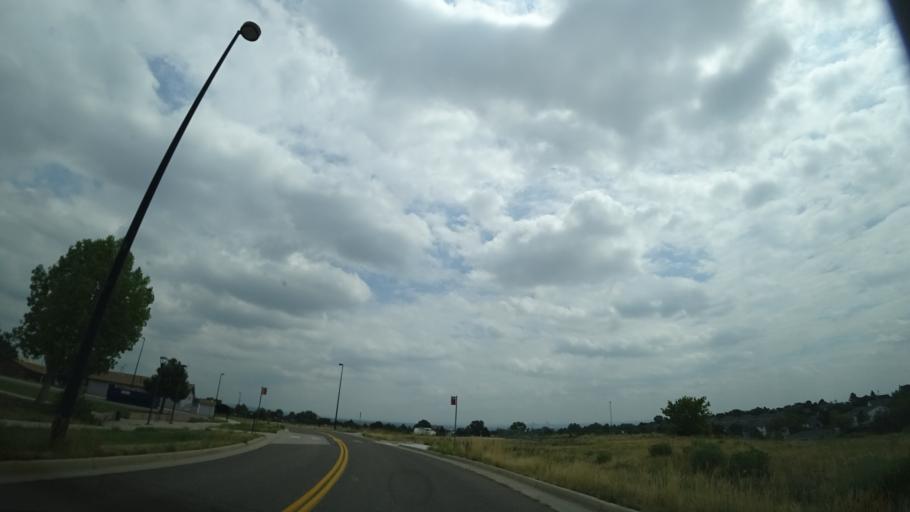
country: US
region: Colorado
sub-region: Jefferson County
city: West Pleasant View
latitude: 39.7138
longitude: -105.1492
